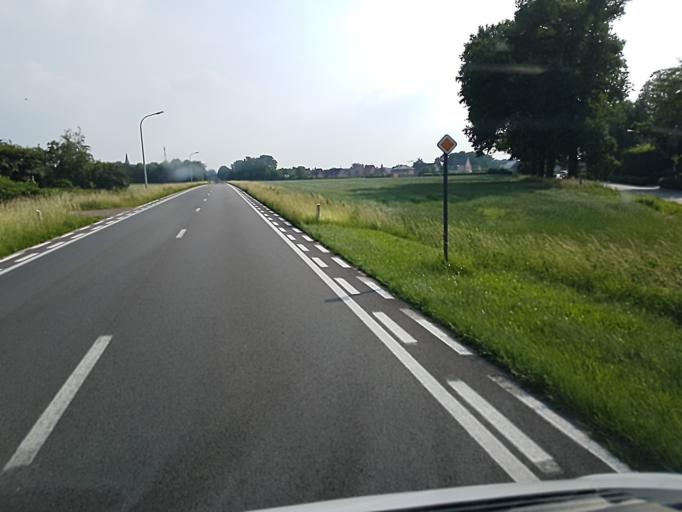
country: BE
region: Flanders
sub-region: Provincie Antwerpen
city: Merksplas
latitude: 51.3673
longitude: 4.8670
